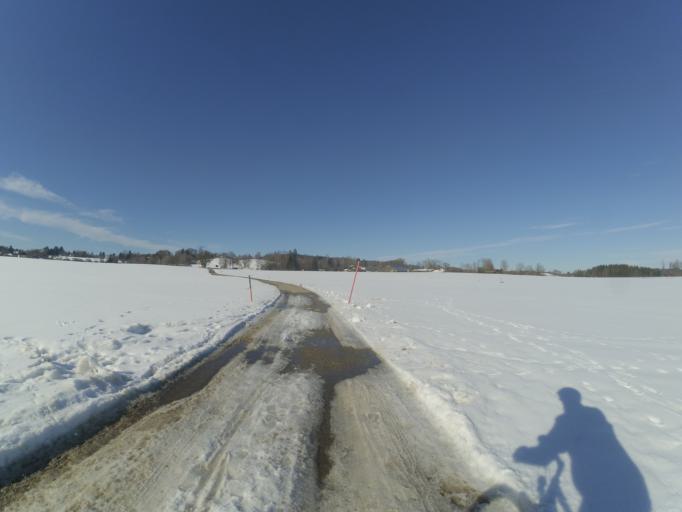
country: DE
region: Bavaria
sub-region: Upper Bavaria
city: Feldkirchen-Westerham
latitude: 47.9111
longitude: 11.8273
